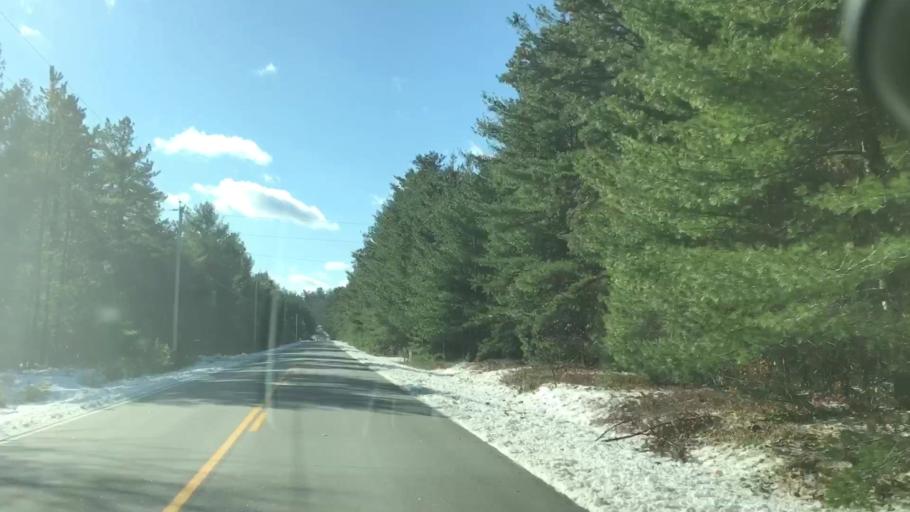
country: US
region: Maine
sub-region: Oxford County
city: Brownfield
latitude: 43.9018
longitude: -70.8862
